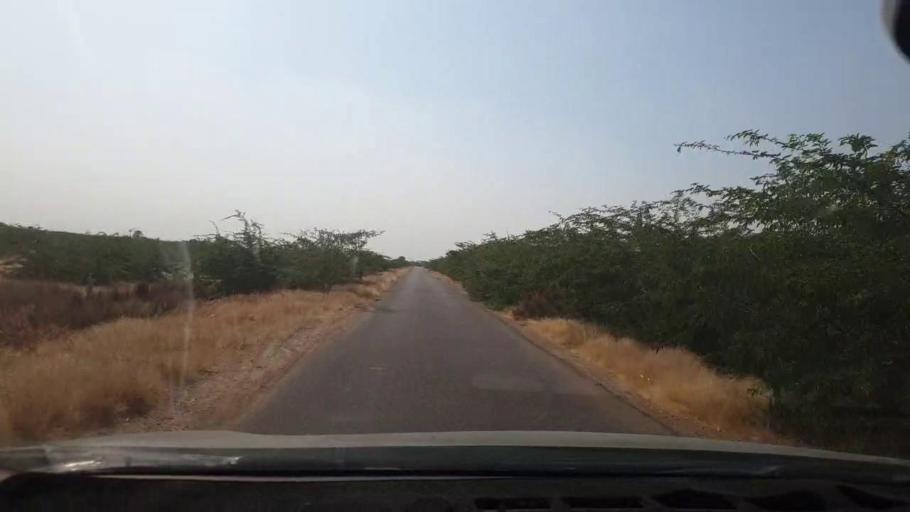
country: PK
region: Sindh
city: Malir Cantonment
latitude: 25.1046
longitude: 67.1985
